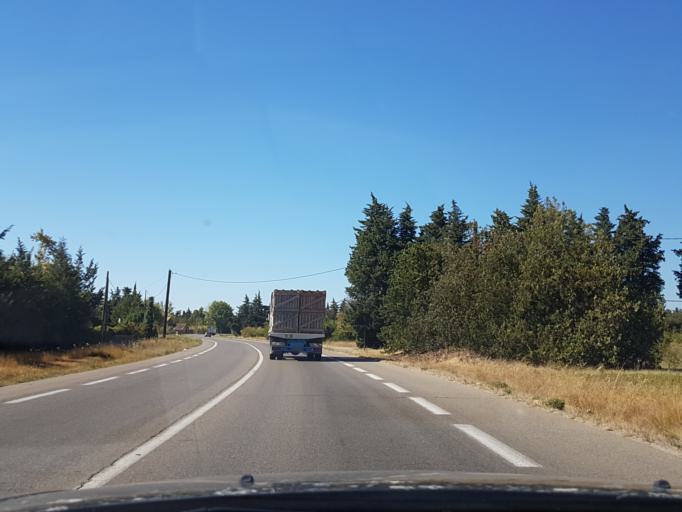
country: FR
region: Provence-Alpes-Cote d'Azur
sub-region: Departement du Vaucluse
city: L'Isle-sur-la-Sorgue
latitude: 43.8993
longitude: 5.0464
